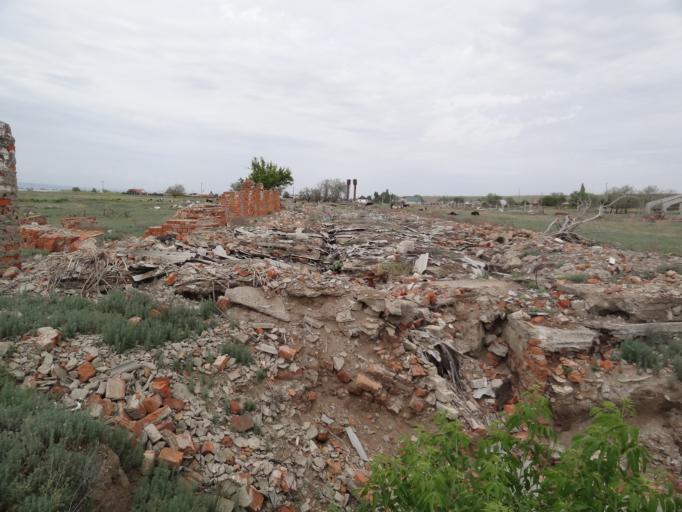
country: RU
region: Saratov
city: Privolzhskiy
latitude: 51.1957
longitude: 45.9125
